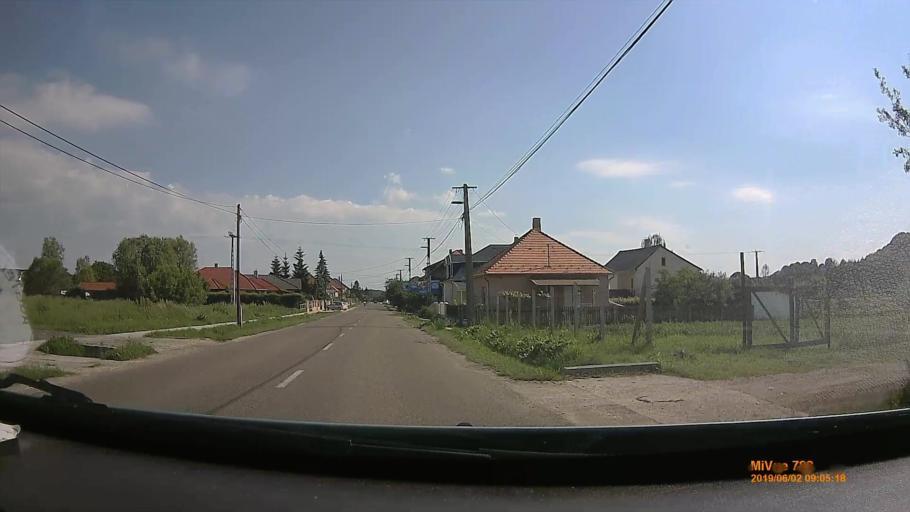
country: HU
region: Borsod-Abauj-Zemplen
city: Kazincbarcika
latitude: 48.1766
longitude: 20.6480
